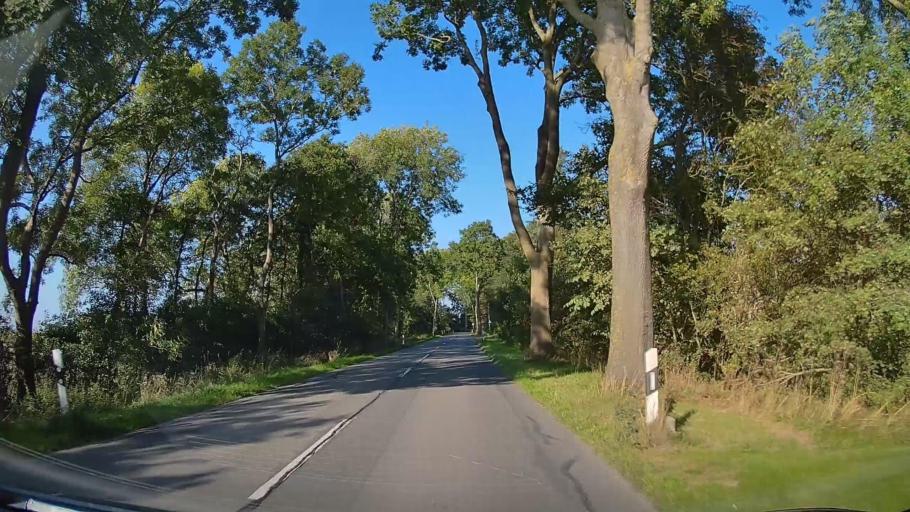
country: DE
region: Lower Saxony
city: Nordholz
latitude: 53.7664
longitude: 8.5687
